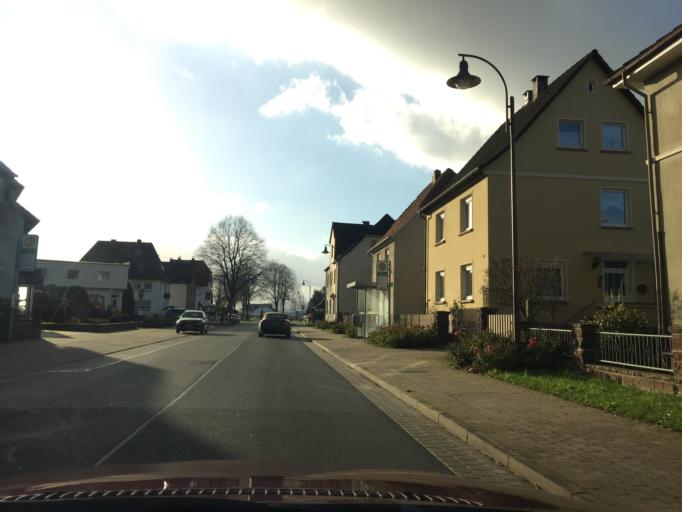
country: DE
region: Lower Saxony
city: Bevern
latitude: 51.8546
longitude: 9.4921
